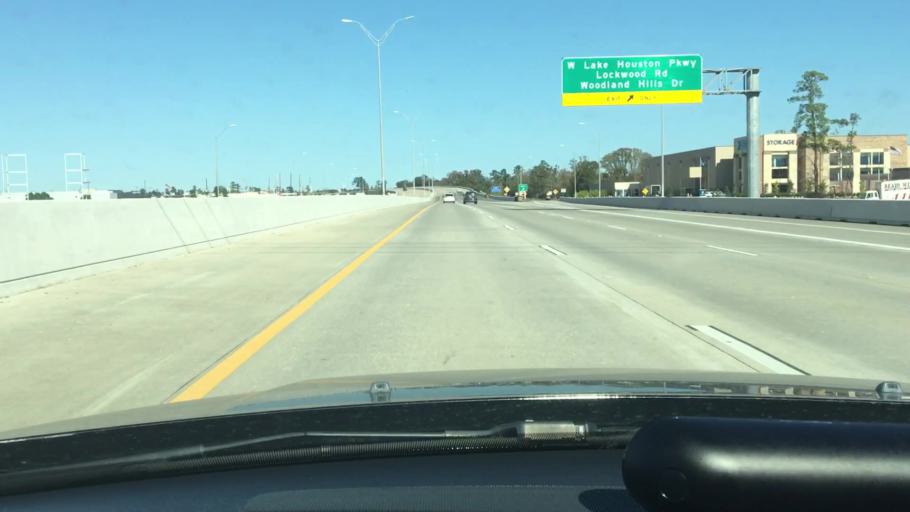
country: US
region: Texas
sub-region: Harris County
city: Atascocita
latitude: 29.9186
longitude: -95.2004
